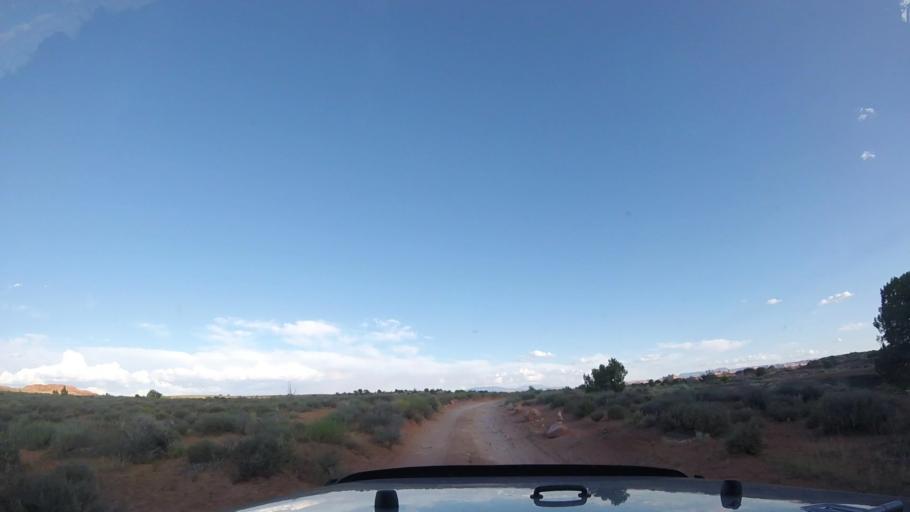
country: US
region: Utah
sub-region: Grand County
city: Moab
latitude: 38.2047
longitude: -109.7849
